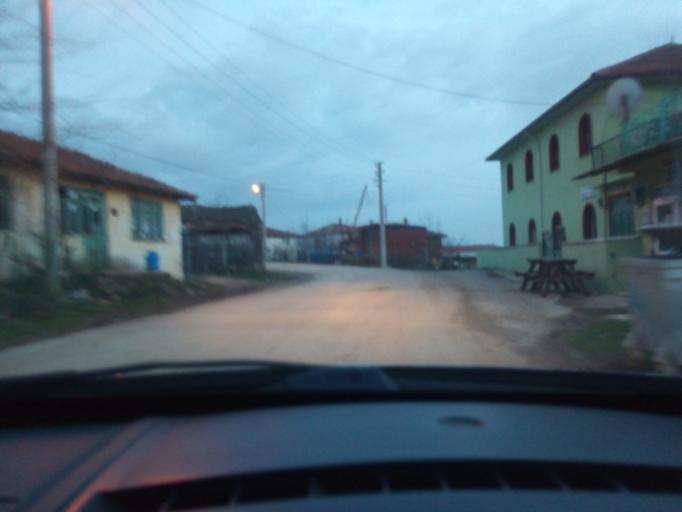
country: TR
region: Balikesir
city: Susurluk
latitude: 39.9169
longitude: 28.0881
